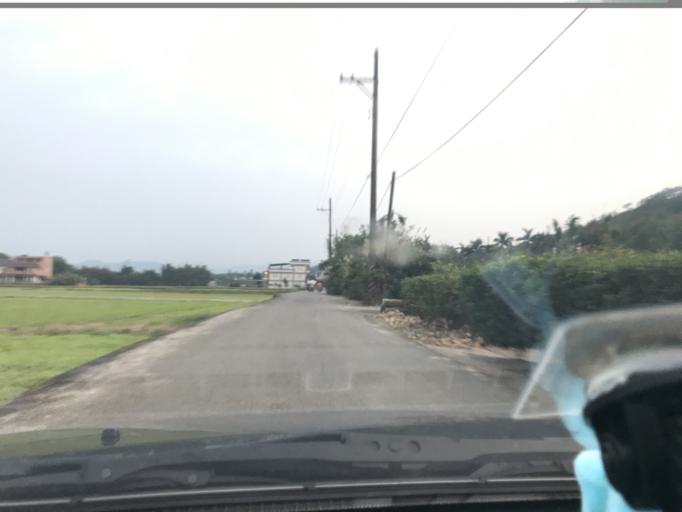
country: TW
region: Taiwan
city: Daxi
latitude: 24.8479
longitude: 121.2107
